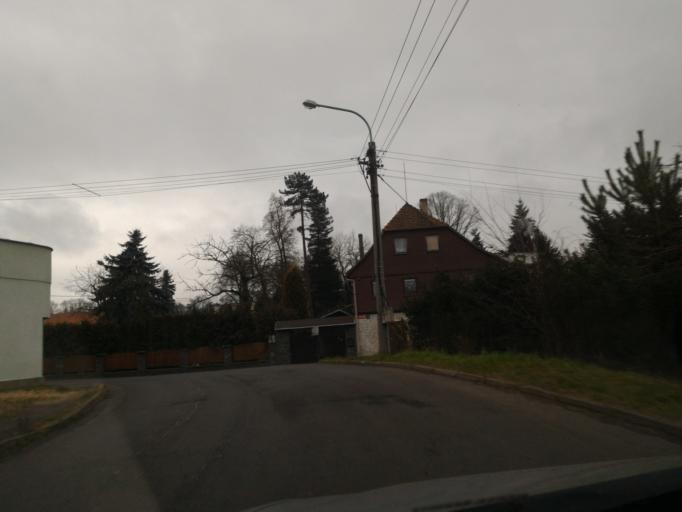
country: CZ
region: Ustecky
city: Varnsdorf
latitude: 50.9152
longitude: 14.6131
